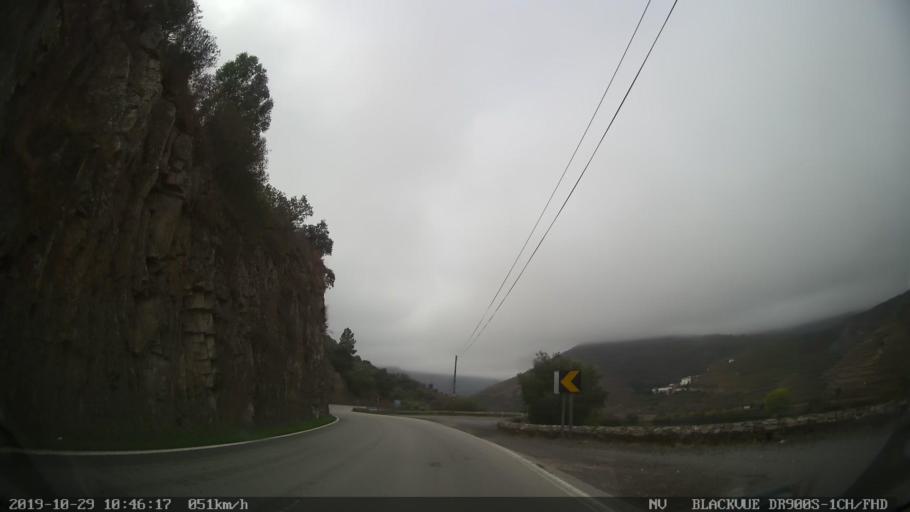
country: PT
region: Viseu
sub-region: Tabuaco
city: Tabuaco
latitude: 41.1662
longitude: -7.5649
